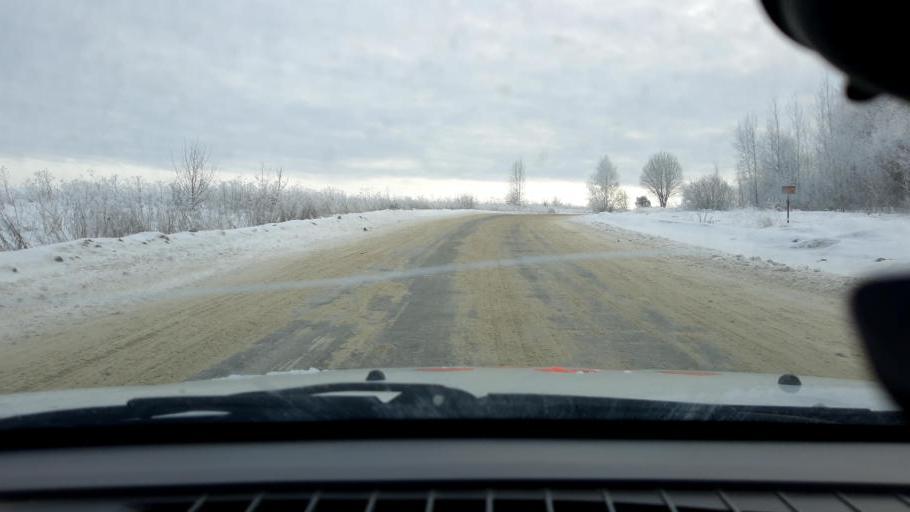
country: RU
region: Nizjnij Novgorod
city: Bogorodsk
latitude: 56.0797
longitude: 43.5748
